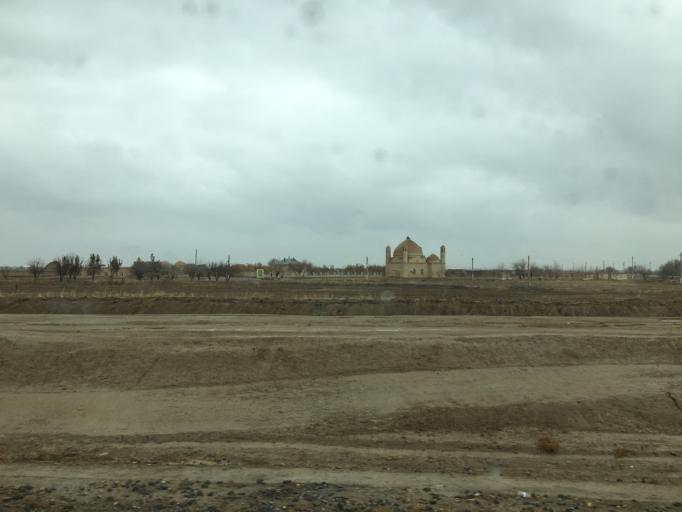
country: TM
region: Mary
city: Bayramaly
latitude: 37.4098
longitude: 62.1684
